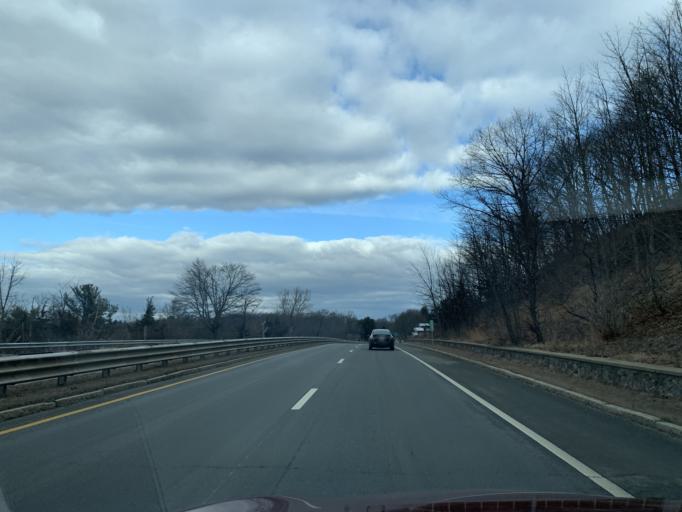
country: US
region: Massachusetts
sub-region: Essex County
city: Newburyport
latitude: 42.8037
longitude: -70.8790
